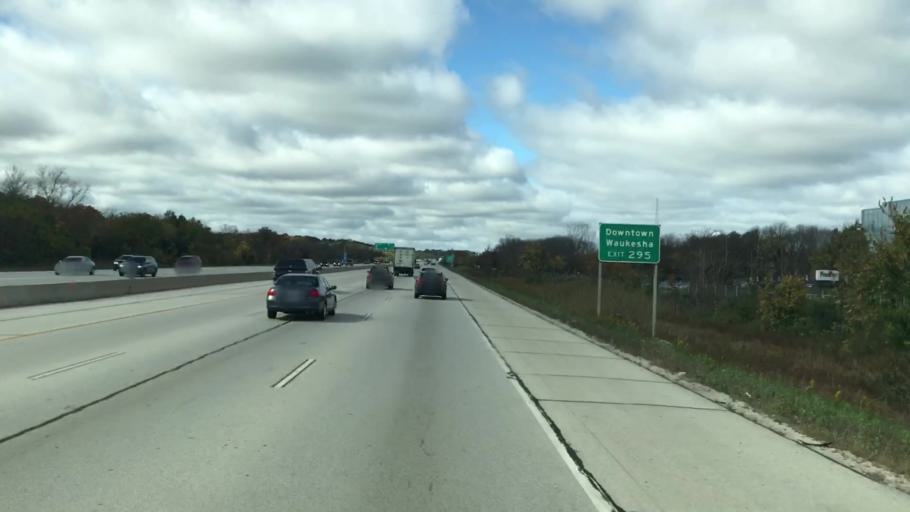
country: US
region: Wisconsin
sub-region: Waukesha County
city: Brookfield
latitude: 43.0291
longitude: -88.1340
